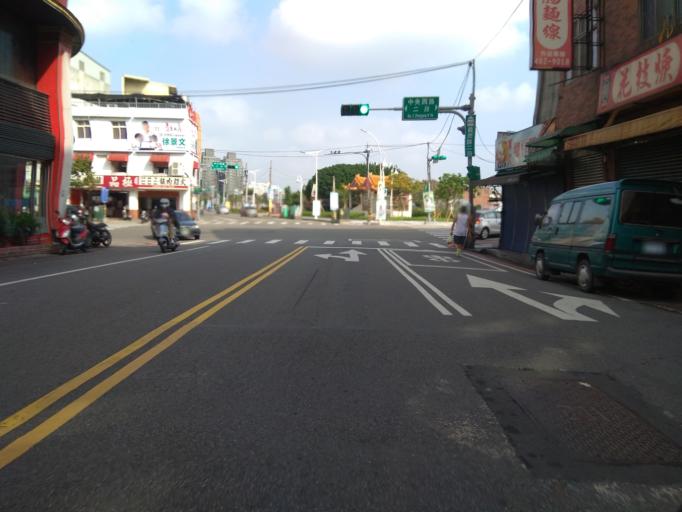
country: TW
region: Taiwan
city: Taoyuan City
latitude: 24.9580
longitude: 121.2183
